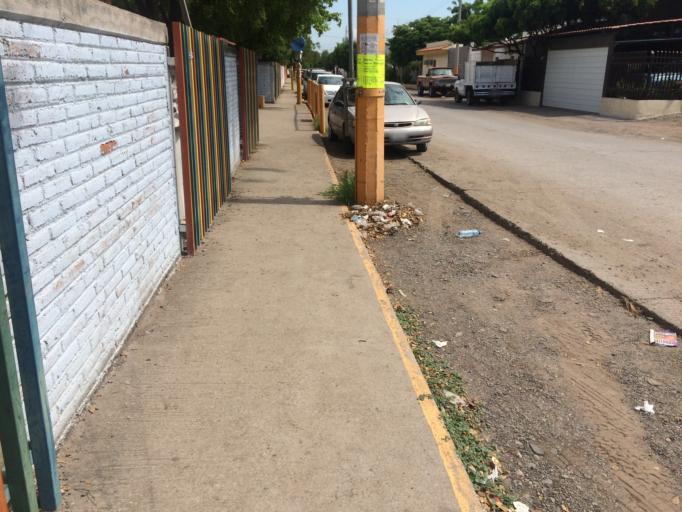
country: MX
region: Sinaloa
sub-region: Culiacan
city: El Diez
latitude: 24.7753
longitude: -107.4775
